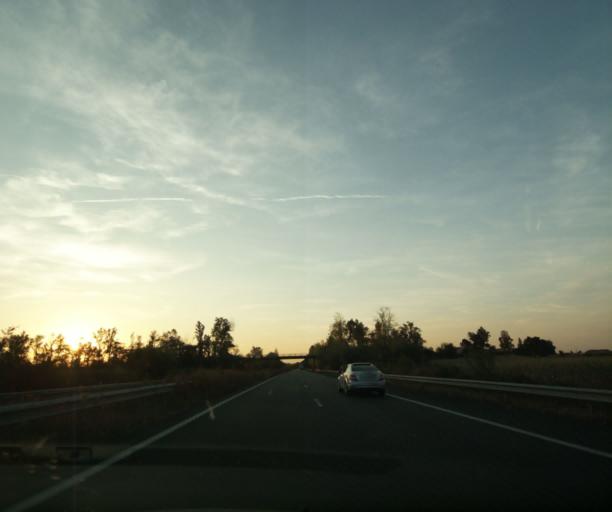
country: FR
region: Aquitaine
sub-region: Departement du Lot-et-Garonne
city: Meilhan-sur-Garonne
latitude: 44.4672
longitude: 0.0617
